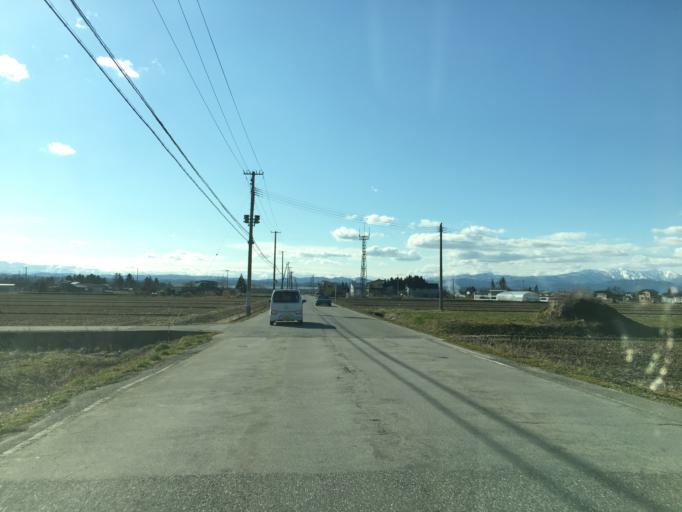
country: JP
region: Yamagata
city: Takahata
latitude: 38.0064
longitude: 140.1008
